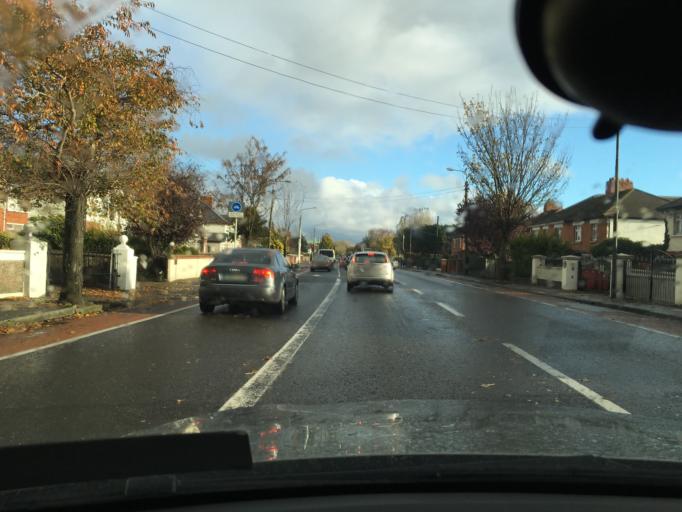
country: IE
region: Leinster
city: Cabra
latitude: 53.3682
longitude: -6.3198
